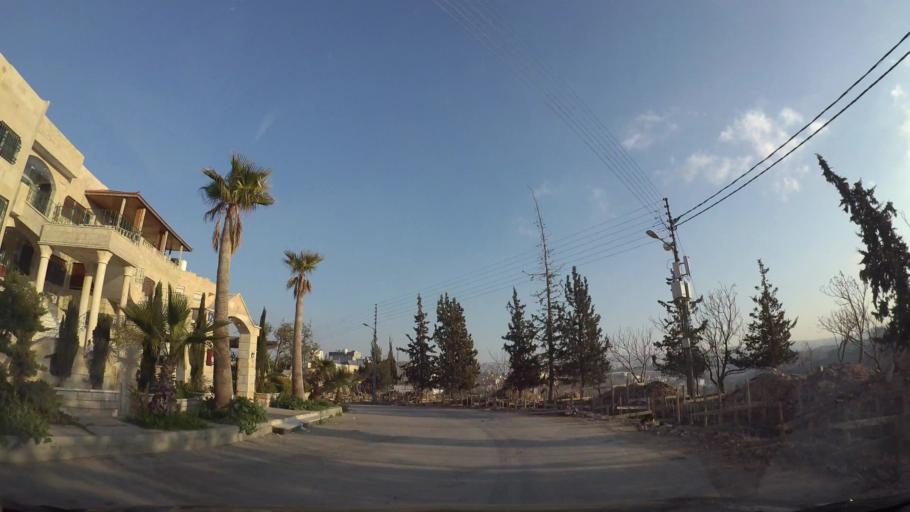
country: JO
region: Amman
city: Amman
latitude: 31.9842
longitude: 35.9715
